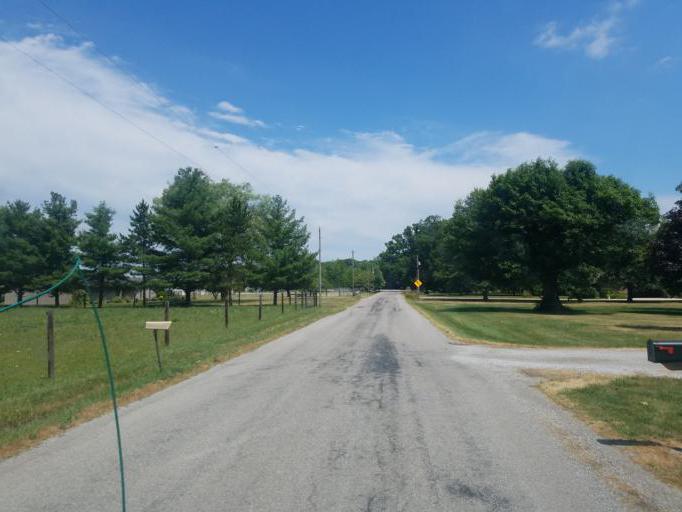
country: US
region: Indiana
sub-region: Allen County
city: Woodburn
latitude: 41.1685
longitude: -84.8575
